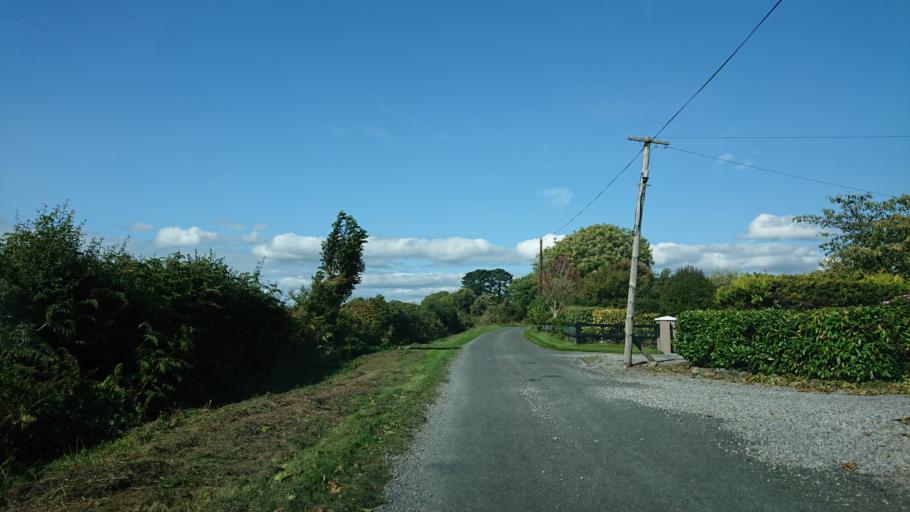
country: IE
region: Munster
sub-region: Waterford
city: Waterford
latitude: 52.2152
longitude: -7.0538
